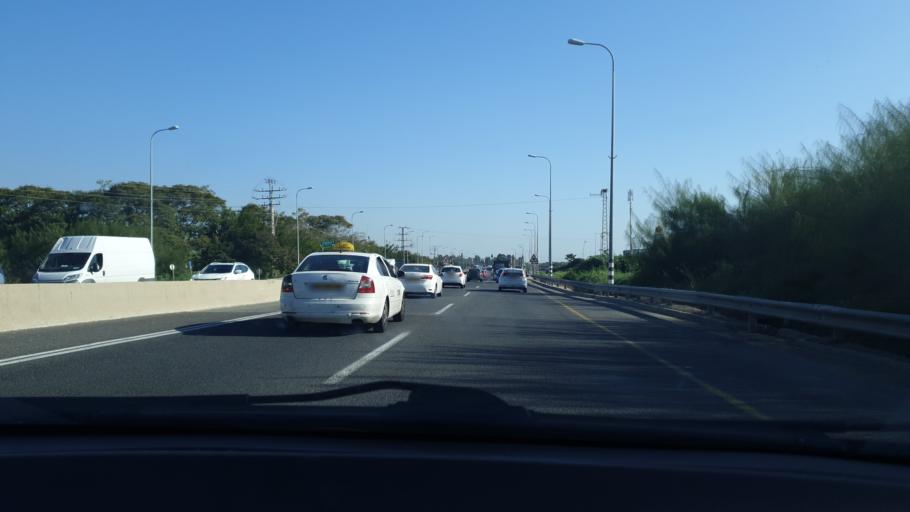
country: IL
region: Central District
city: Kefar Habad
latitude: 31.9617
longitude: 34.8500
